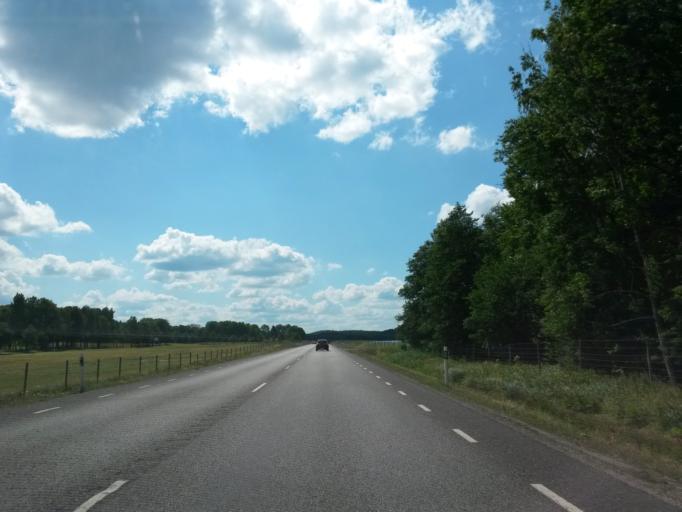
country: SE
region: Vaestra Goetaland
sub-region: Alingsas Kommun
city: Ingared
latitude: 57.9581
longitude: 12.3977
